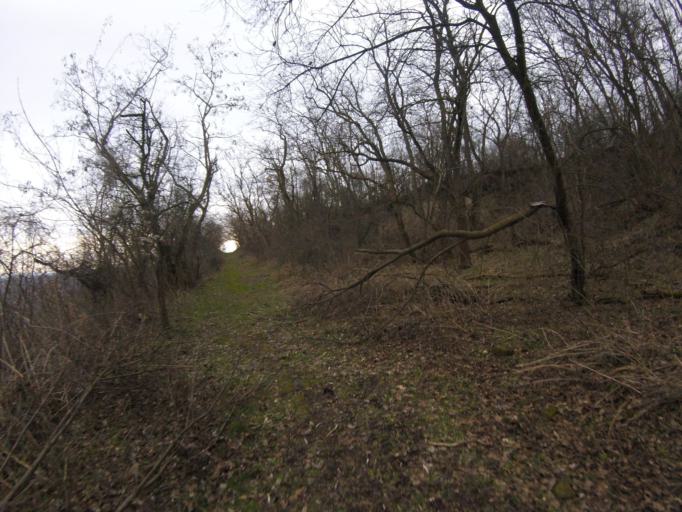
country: HU
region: Heves
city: Egerszalok
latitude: 47.8333
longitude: 20.3378
